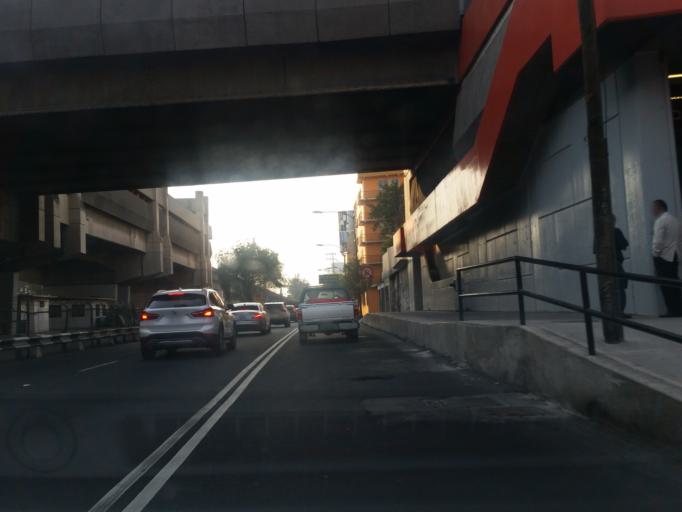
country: MX
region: Mexico City
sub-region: Iztacalco
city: Iztacalco
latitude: 19.4086
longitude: -99.0909
